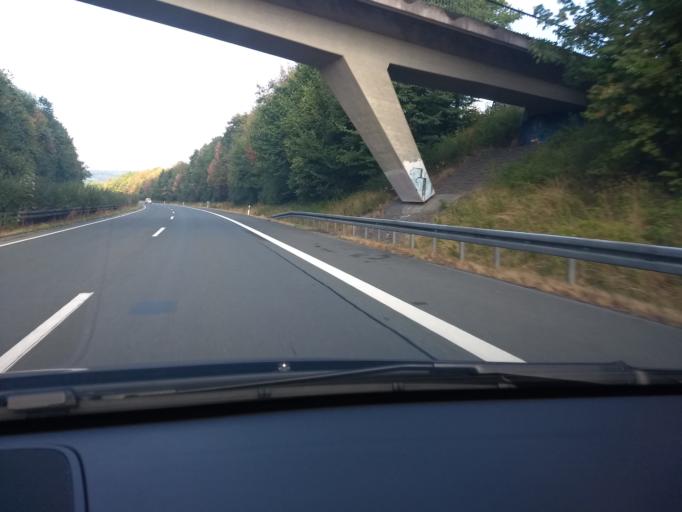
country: DE
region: North Rhine-Westphalia
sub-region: Regierungsbezirk Arnsberg
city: Meschede
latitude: 51.3648
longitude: 8.3237
